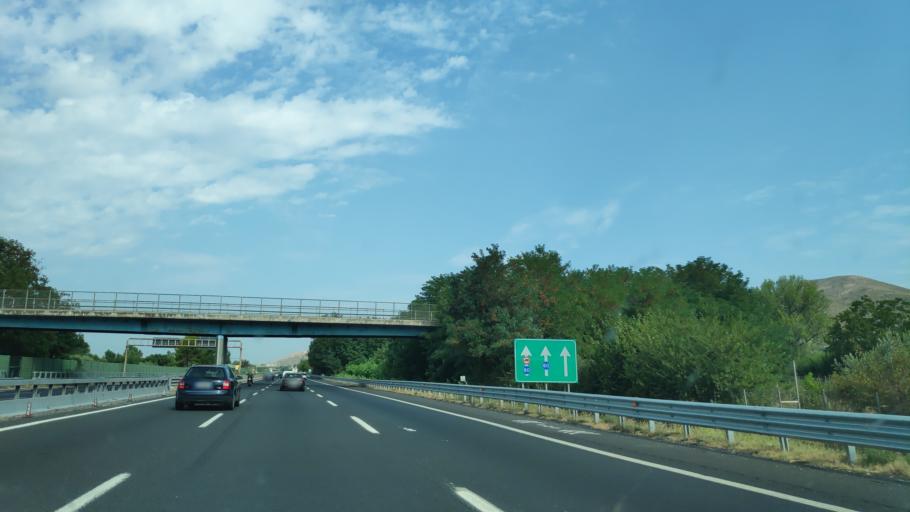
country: IT
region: Campania
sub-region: Provincia di Caserta
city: Casapulla
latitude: 41.0788
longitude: 14.2958
